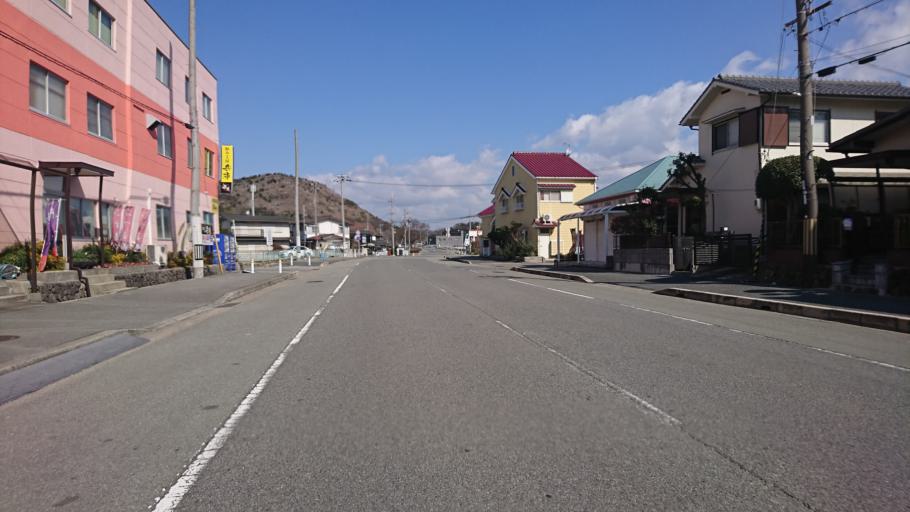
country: JP
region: Hyogo
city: Kakogawacho-honmachi
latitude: 34.7929
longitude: 134.8066
